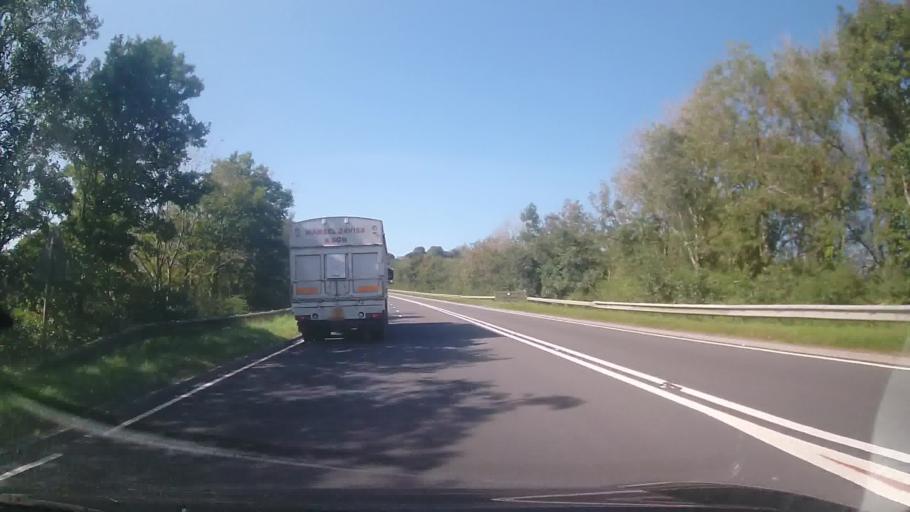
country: GB
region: Wales
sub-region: Carmarthenshire
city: Whitland
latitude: 51.8208
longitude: -4.6470
